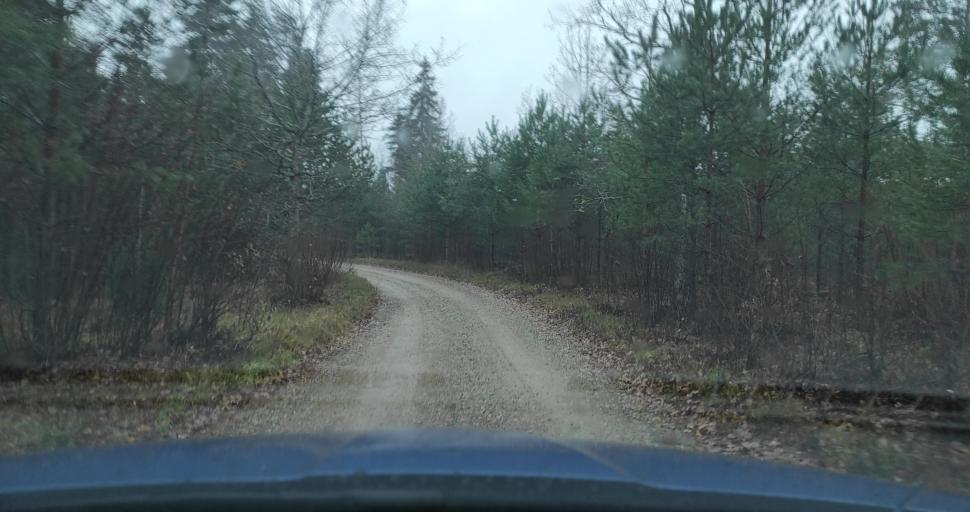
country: LV
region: Alsunga
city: Alsunga
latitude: 56.8930
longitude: 21.5841
